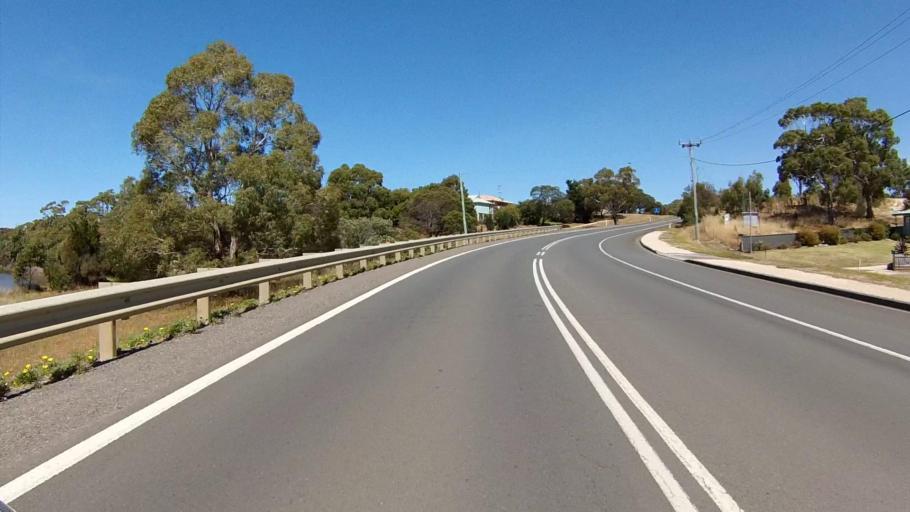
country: AU
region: Tasmania
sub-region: Sorell
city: Sorell
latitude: -42.1306
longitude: 148.0725
